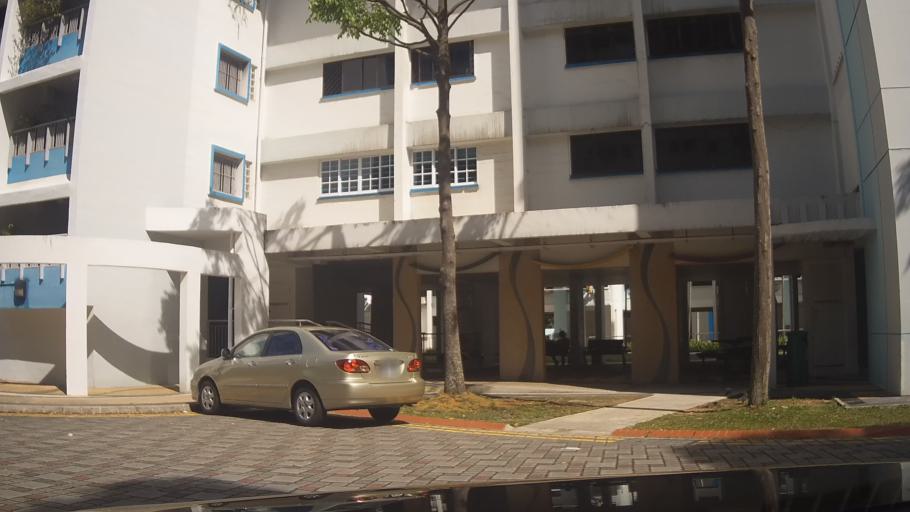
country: MY
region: Johor
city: Johor Bahru
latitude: 1.4434
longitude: 103.7725
